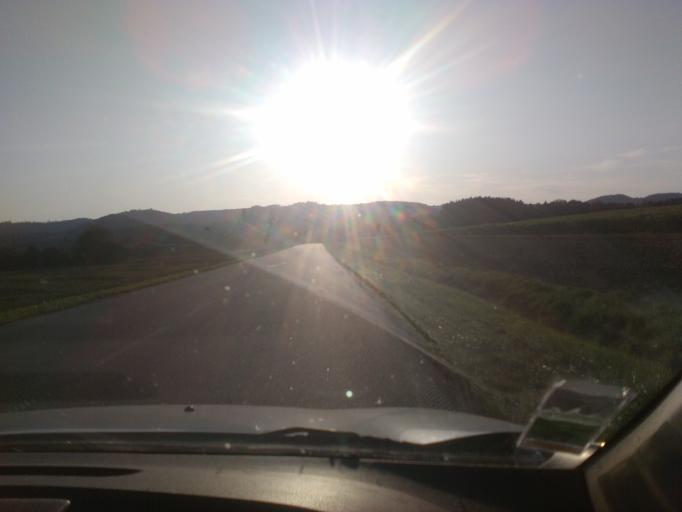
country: FR
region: Lorraine
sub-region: Departement des Vosges
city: Etival-Clairefontaine
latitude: 48.3222
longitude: 6.8405
